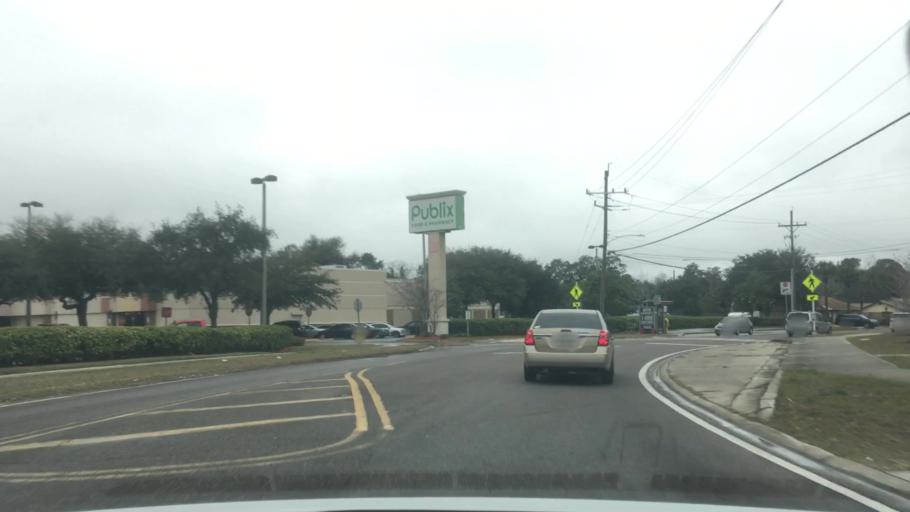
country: US
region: Florida
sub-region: Duval County
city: Jacksonville
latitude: 30.3530
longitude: -81.5778
